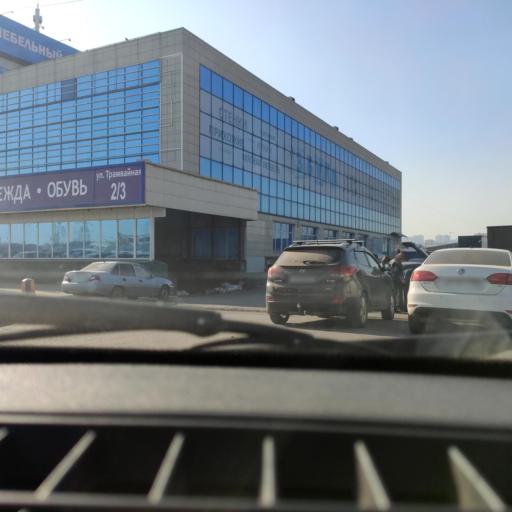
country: RU
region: Bashkortostan
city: Ufa
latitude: 54.7973
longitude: 56.0756
